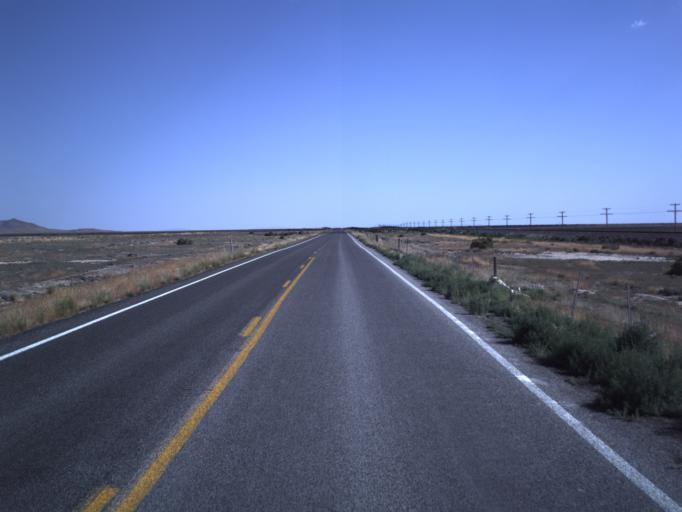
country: US
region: Utah
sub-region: Millard County
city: Delta
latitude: 38.9414
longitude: -112.8078
